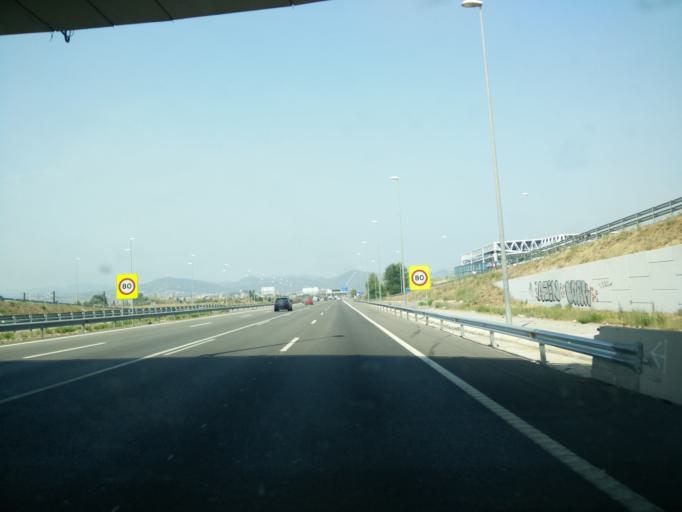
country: ES
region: Catalonia
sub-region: Provincia de Barcelona
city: Cornella de Llobregat
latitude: 41.3457
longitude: 2.0800
